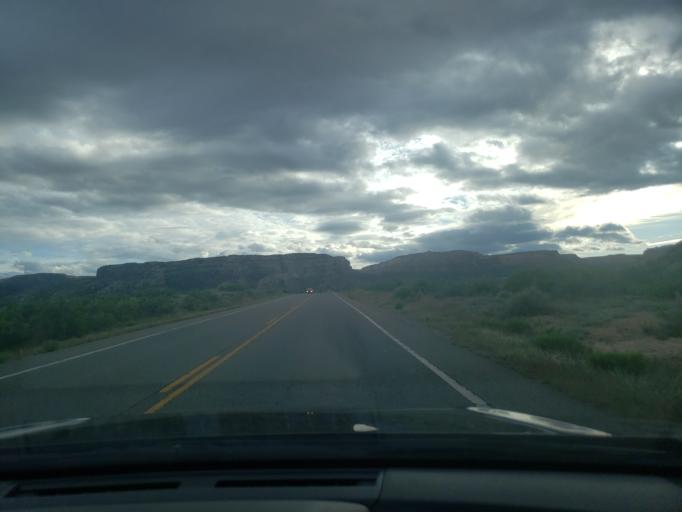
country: US
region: Colorado
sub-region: Mesa County
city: Redlands
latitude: 39.0477
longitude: -108.6144
